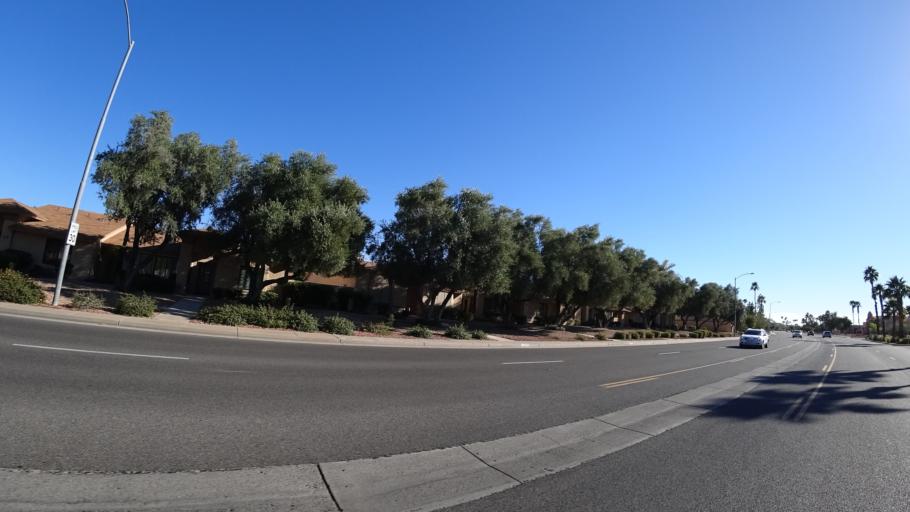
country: US
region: Arizona
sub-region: Maricopa County
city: Sun City West
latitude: 33.6676
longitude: -112.3561
